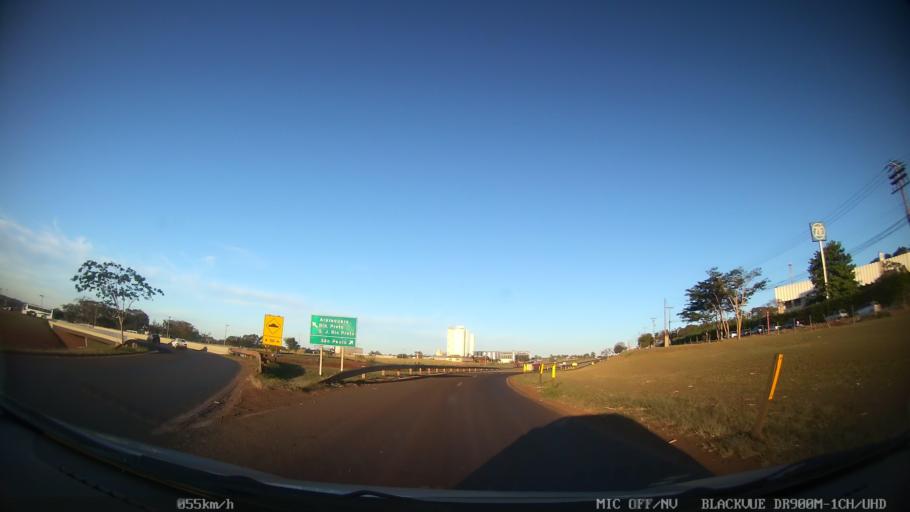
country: BR
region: Sao Paulo
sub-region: Araraquara
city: Araraquara
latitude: -21.8196
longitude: -48.1779
